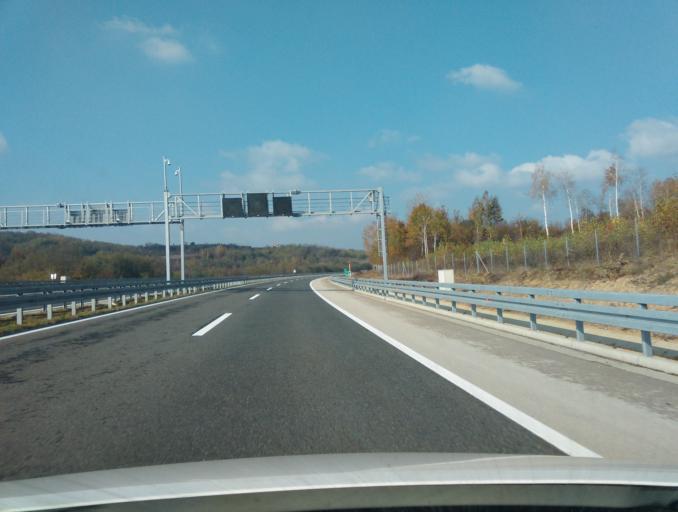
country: BA
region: Republika Srpska
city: Doboj
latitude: 44.8319
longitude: 17.9889
